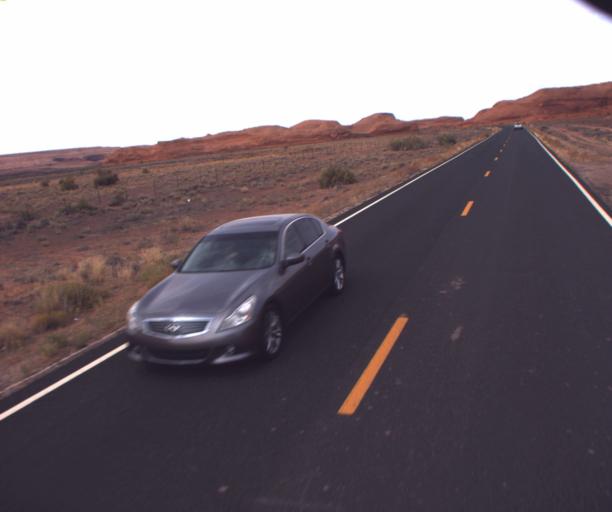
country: US
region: Arizona
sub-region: Apache County
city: Many Farms
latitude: 36.7628
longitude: -109.6513
